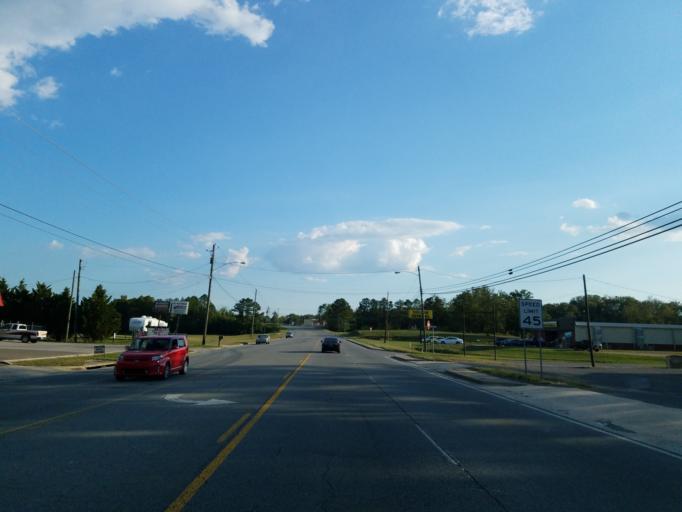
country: US
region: Georgia
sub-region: Murray County
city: Chatsworth
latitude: 34.7566
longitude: -84.7695
